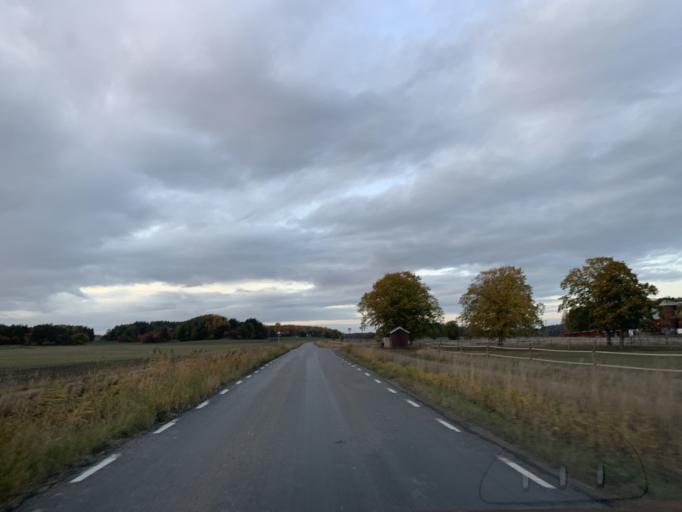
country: SE
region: Stockholm
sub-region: Nynashamns Kommun
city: Osmo
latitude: 58.9057
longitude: 17.7887
